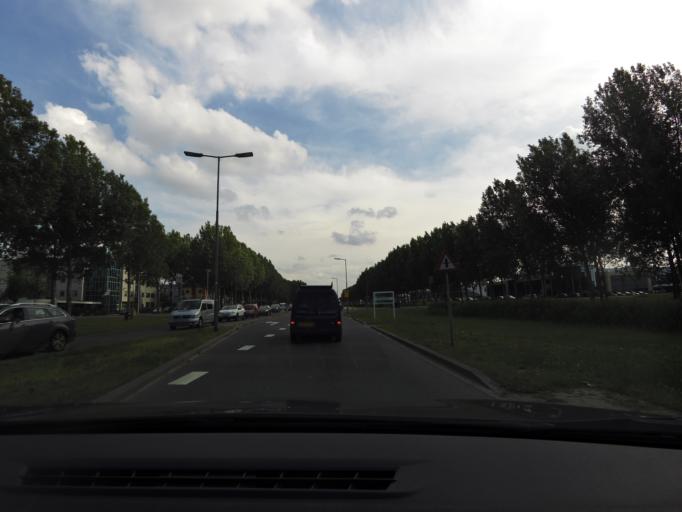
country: NL
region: South Holland
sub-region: Gemeente Schiedam
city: Schiedam
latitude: 51.9443
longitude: 4.4085
